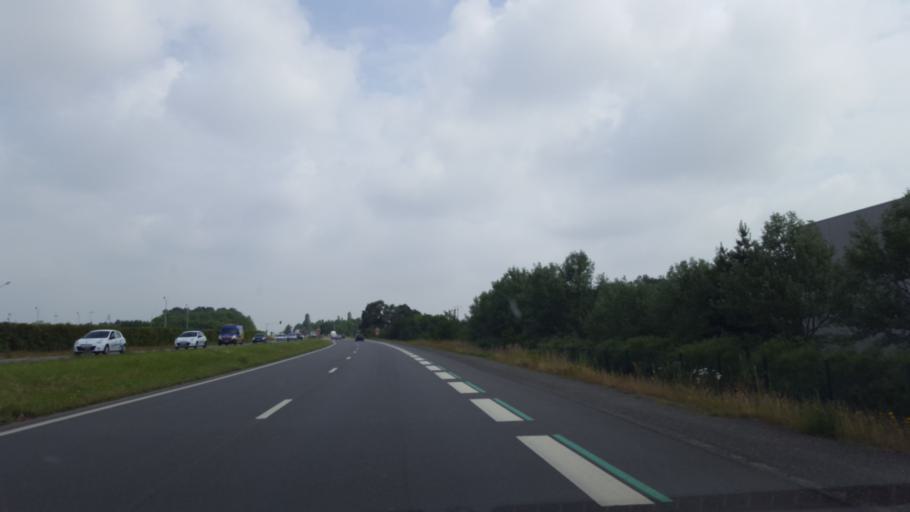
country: FR
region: Brittany
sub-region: Departement d'Ille-et-Vilaine
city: Saint-Jacques-de-la-Lande
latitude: 48.0598
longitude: -1.7005
